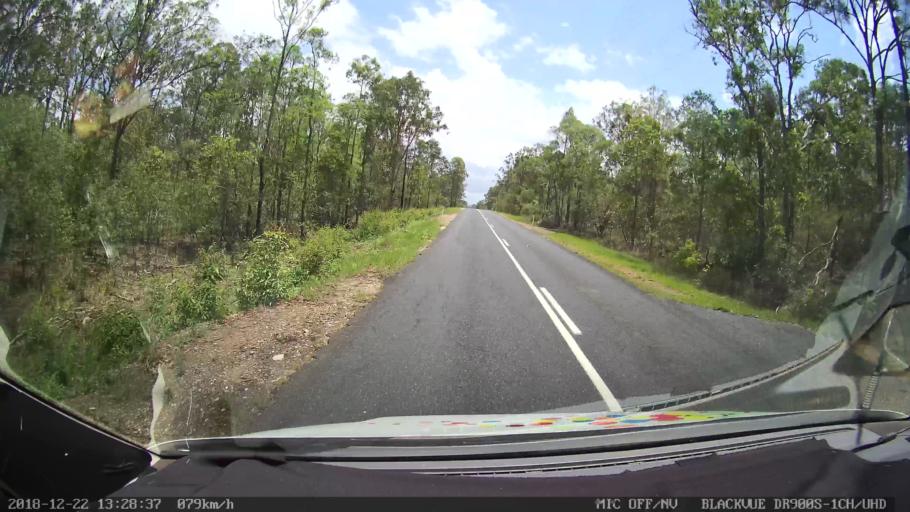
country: AU
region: New South Wales
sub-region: Clarence Valley
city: Coutts Crossing
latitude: -29.8354
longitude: 152.8864
